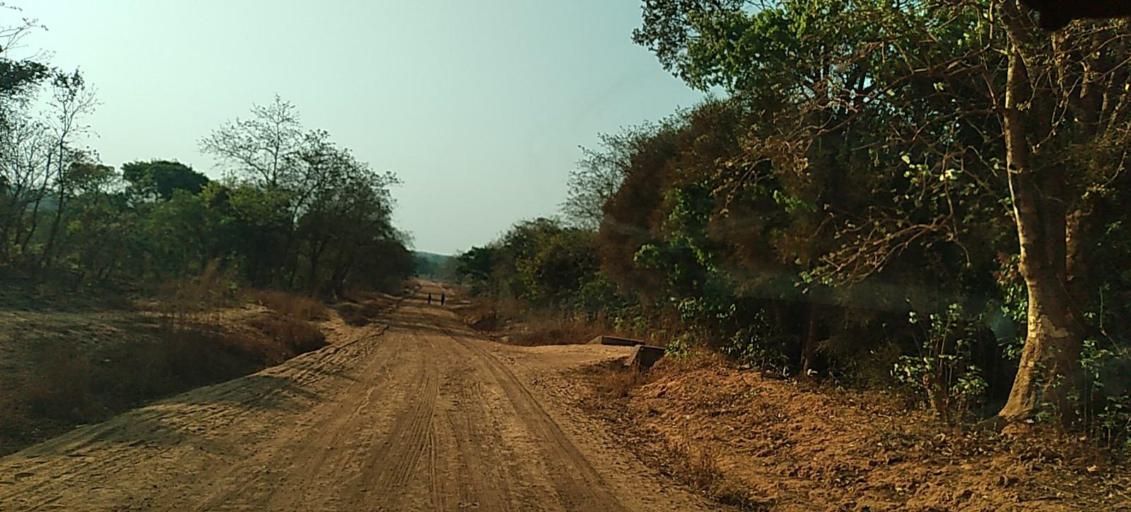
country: ZM
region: North-Western
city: Kasempa
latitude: -13.5145
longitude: 25.9351
